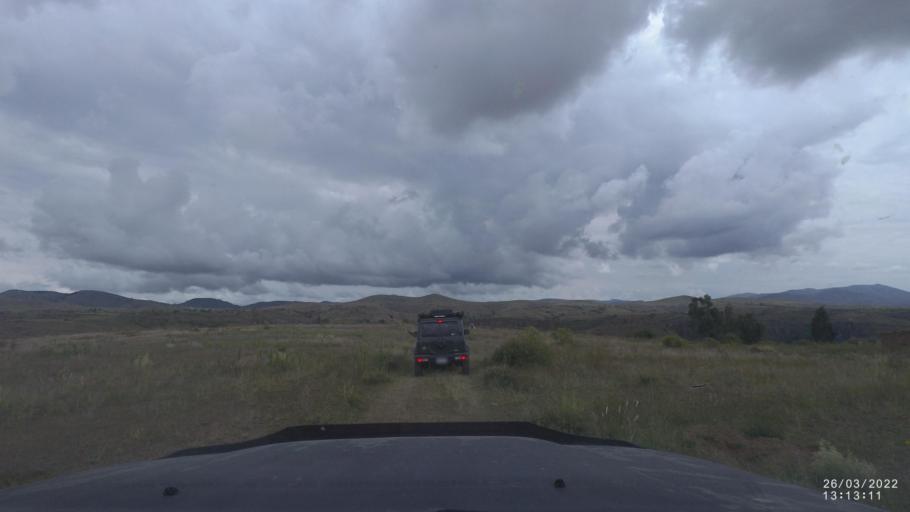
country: BO
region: Cochabamba
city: Cliza
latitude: -17.7383
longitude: -65.8629
